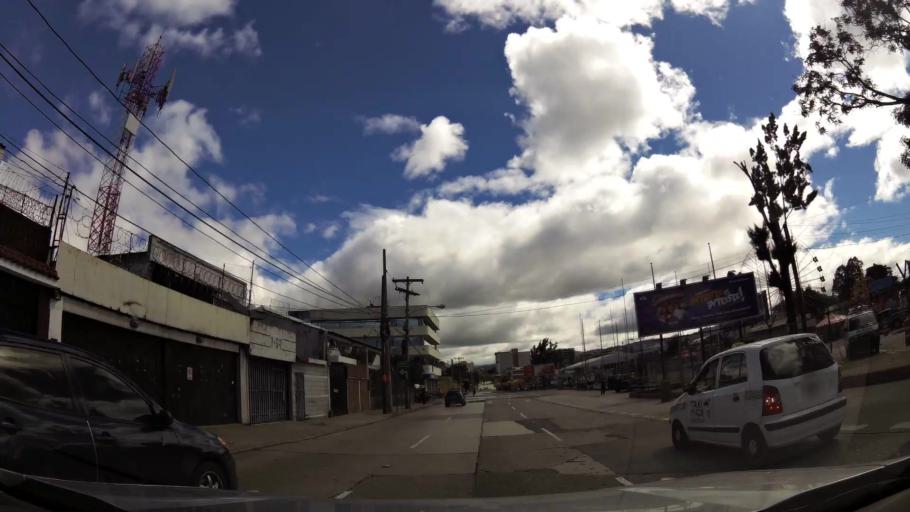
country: GT
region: Guatemala
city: Guatemala City
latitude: 14.6102
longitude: -90.5239
